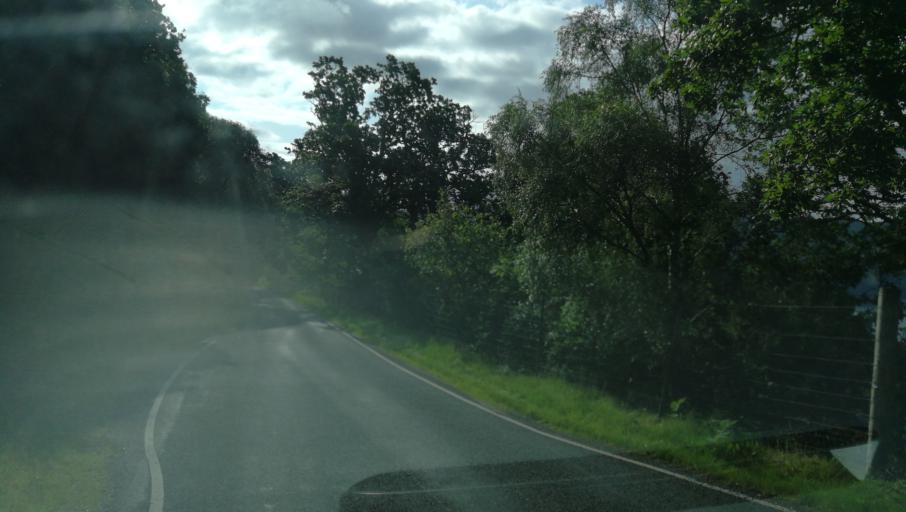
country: GB
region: Scotland
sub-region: Argyll and Bute
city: Isle Of Mull
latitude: 56.6814
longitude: -5.8598
